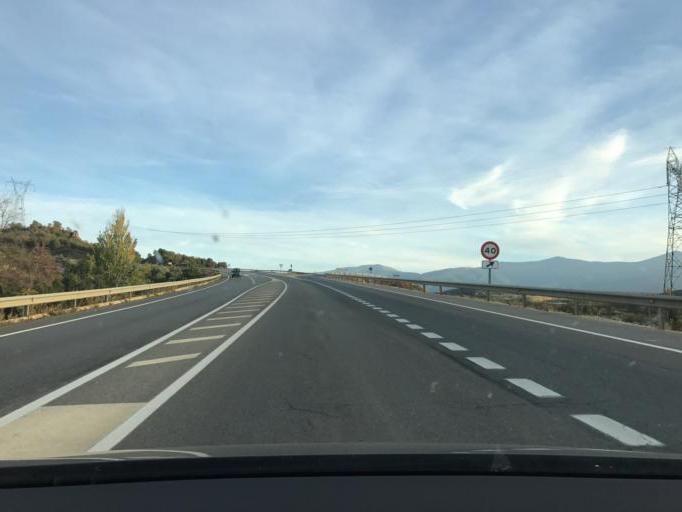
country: ES
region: Andalusia
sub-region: Provincia de Granada
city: Guadix
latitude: 37.2752
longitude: -3.1101
